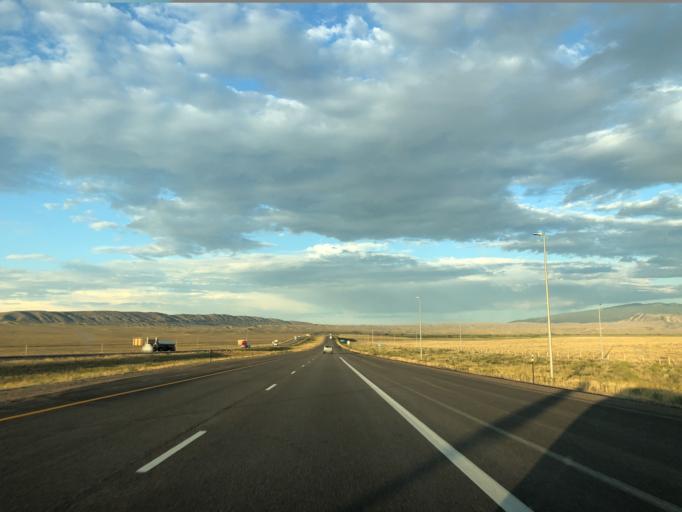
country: US
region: Wyoming
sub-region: Carbon County
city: Saratoga
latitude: 41.7411
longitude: -106.8210
